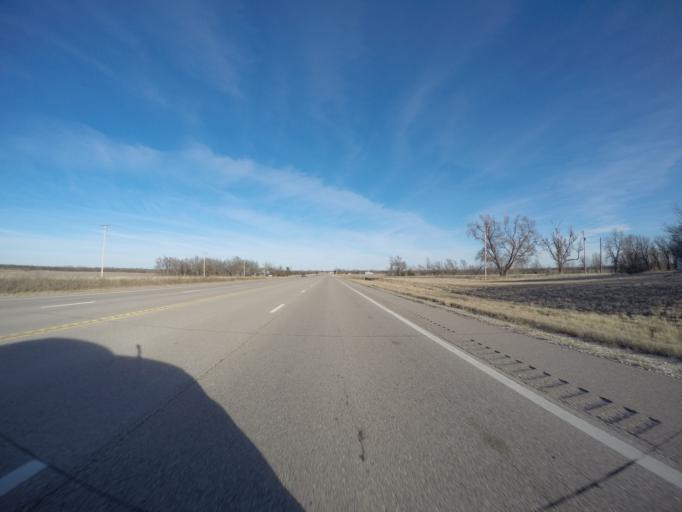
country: US
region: Kansas
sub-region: Marion County
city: Peabody
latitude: 38.1746
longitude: -97.1394
